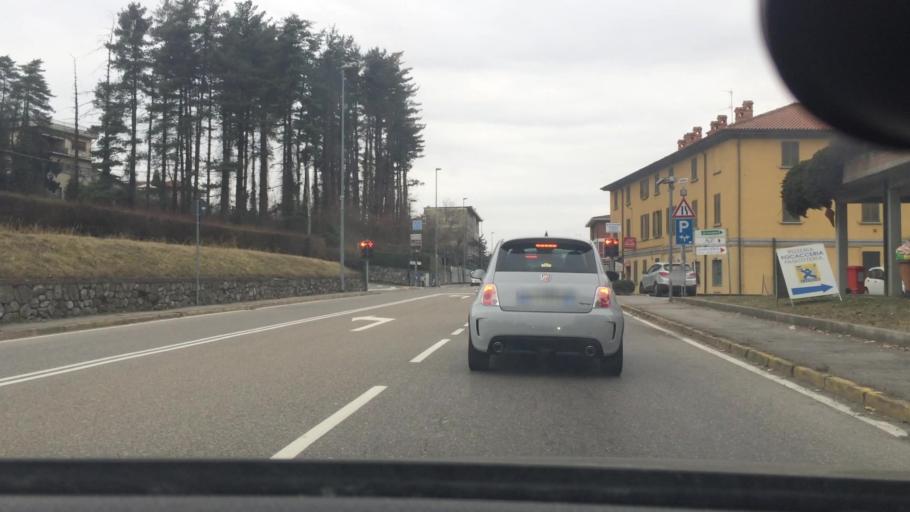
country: IT
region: Lombardy
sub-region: Provincia di Como
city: Lurago d'Erba
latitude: 45.7542
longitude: 9.2236
